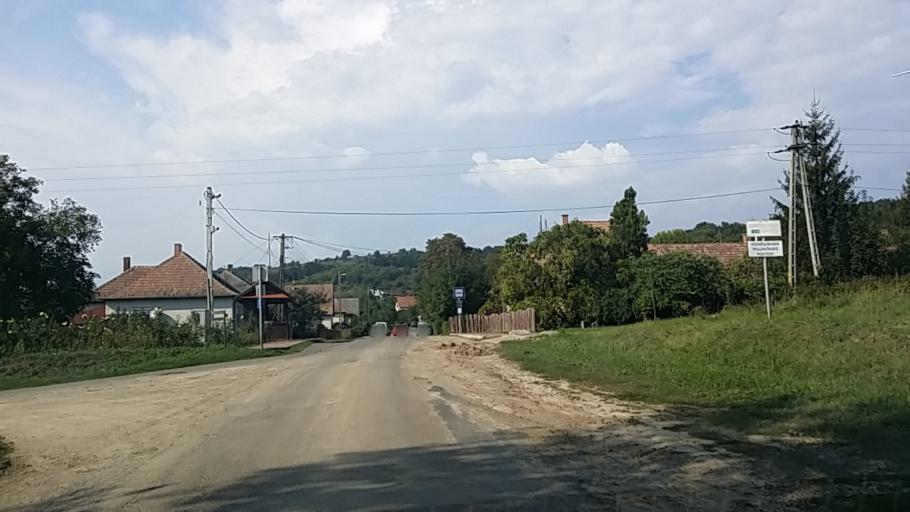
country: HU
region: Nograd
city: Bujak
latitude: 47.8600
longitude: 19.5111
